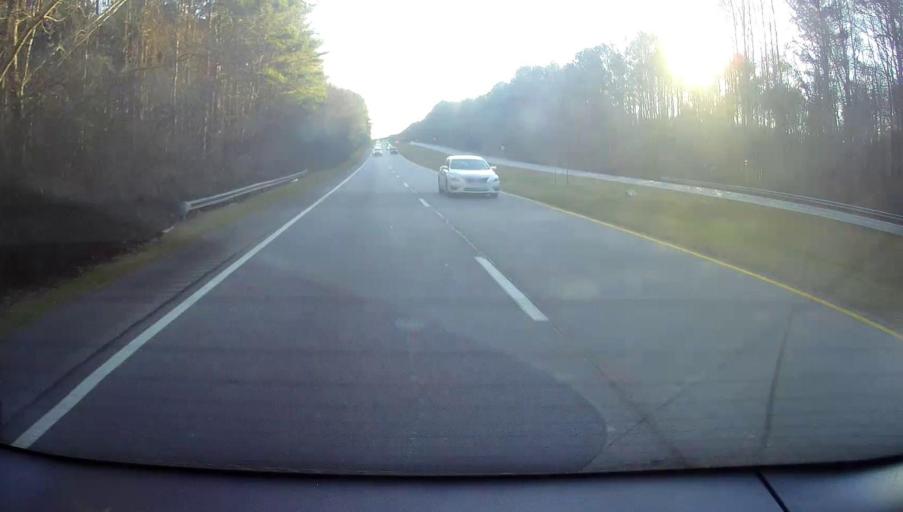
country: US
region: Georgia
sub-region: Fayette County
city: Peachtree City
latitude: 33.4338
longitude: -84.5975
